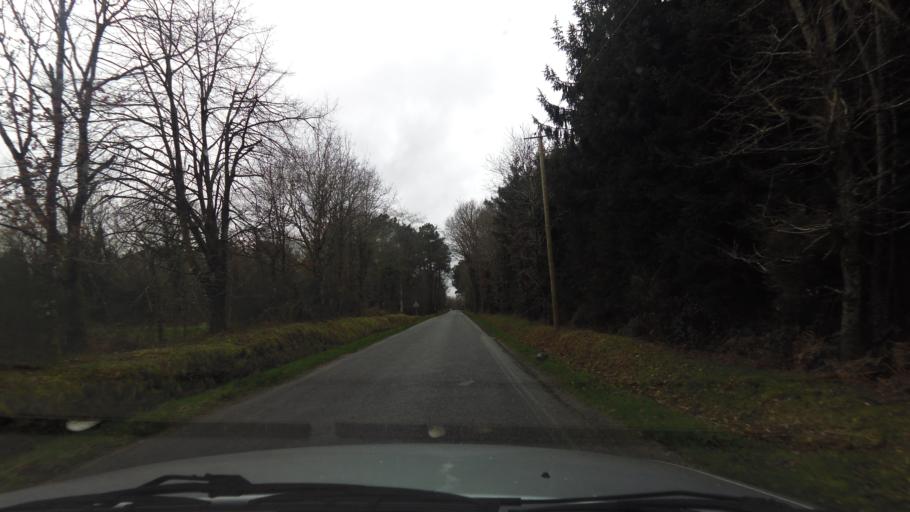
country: FR
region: Brittany
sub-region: Departement du Morbihan
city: Elven
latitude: 47.7831
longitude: -2.5591
